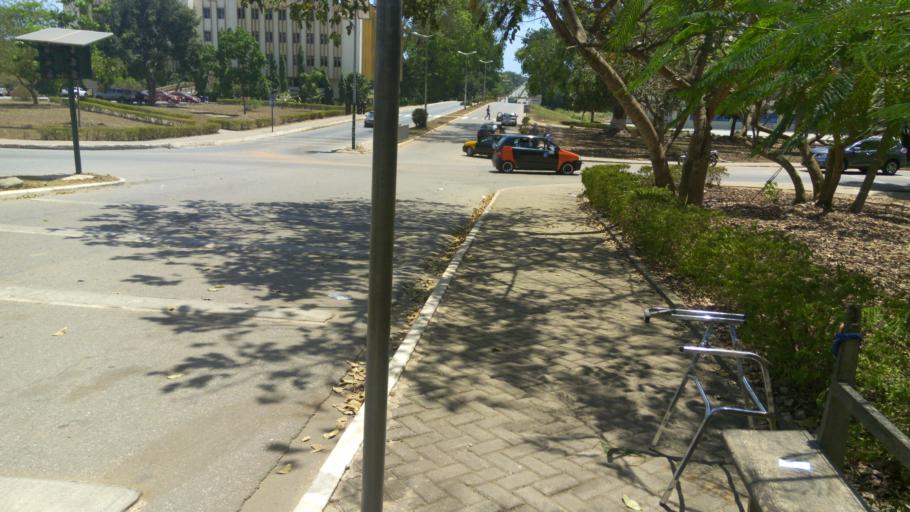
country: GH
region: Central
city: Cape Coast
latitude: 5.1163
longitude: -1.2924
